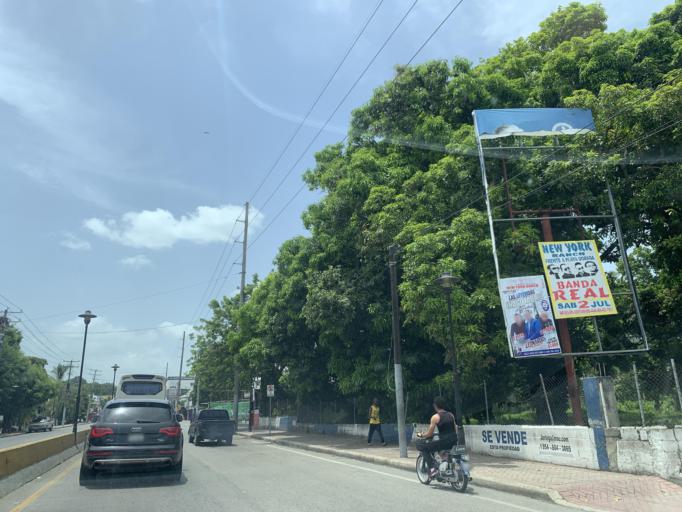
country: DO
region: Puerto Plata
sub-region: Puerto Plata
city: Puerto Plata
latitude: 19.7899
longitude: -70.6998
